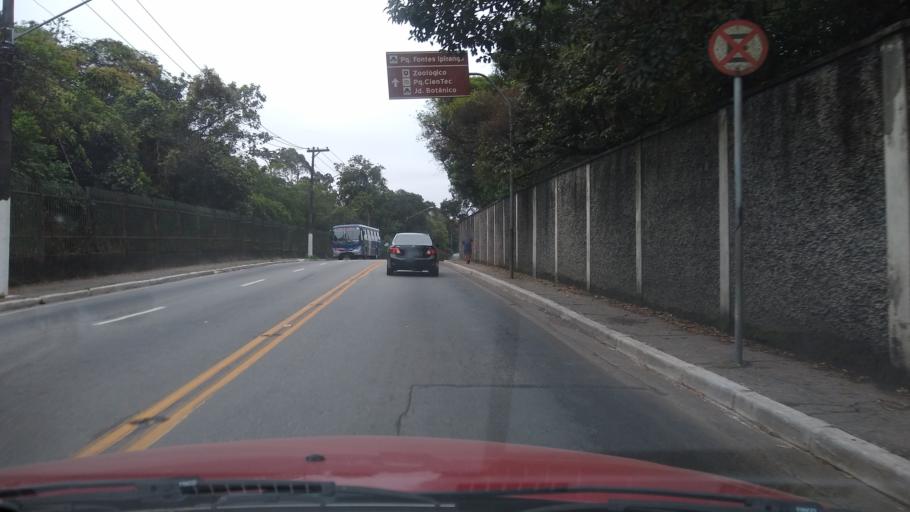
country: BR
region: Sao Paulo
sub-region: Diadema
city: Diadema
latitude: -23.6564
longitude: -46.6166
